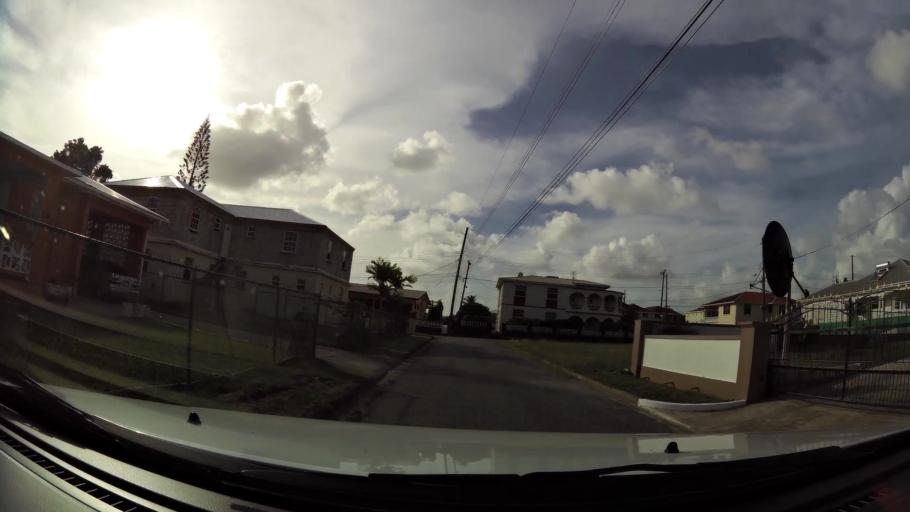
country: BB
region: Christ Church
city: Oistins
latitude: 13.0807
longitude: -59.5681
